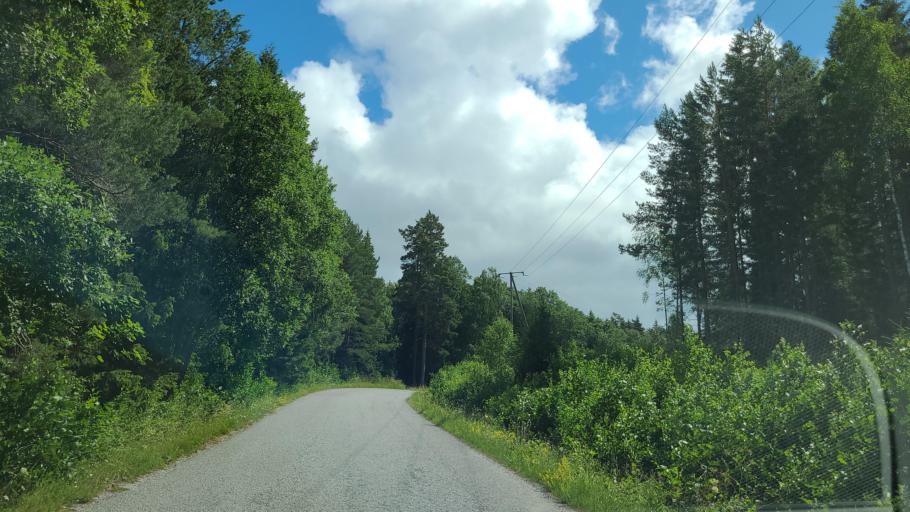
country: FI
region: Varsinais-Suomi
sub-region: Aboland-Turunmaa
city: Nagu
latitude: 60.1824
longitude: 22.0211
